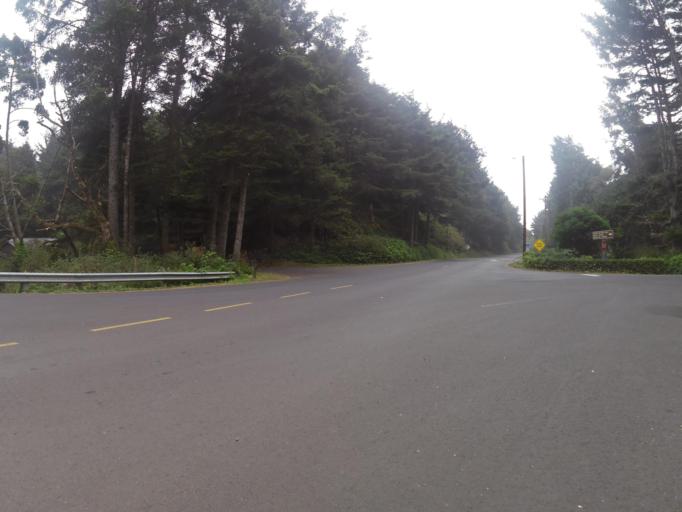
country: US
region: Oregon
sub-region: Lincoln County
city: Depoe Bay
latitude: 44.7285
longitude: -124.0555
